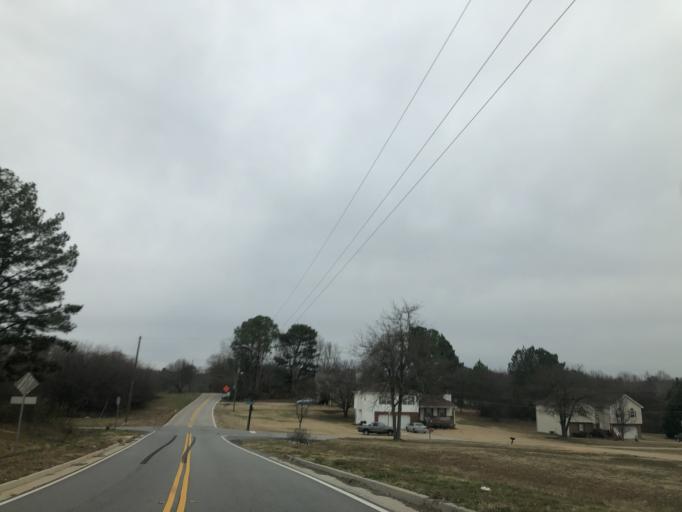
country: US
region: Georgia
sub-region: Clayton County
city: Conley
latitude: 33.6267
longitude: -84.2793
